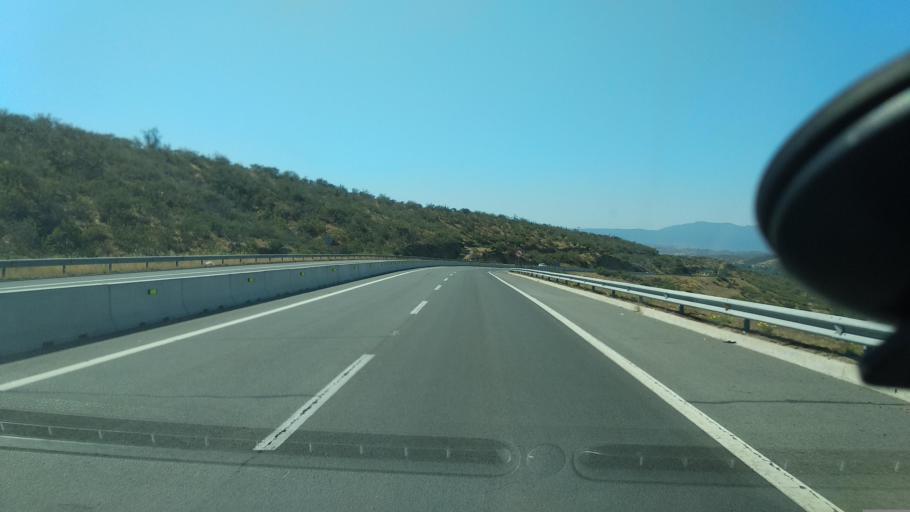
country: CL
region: Valparaiso
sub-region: Provincia de Marga Marga
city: Villa Alemana
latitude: -33.0395
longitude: -71.3189
